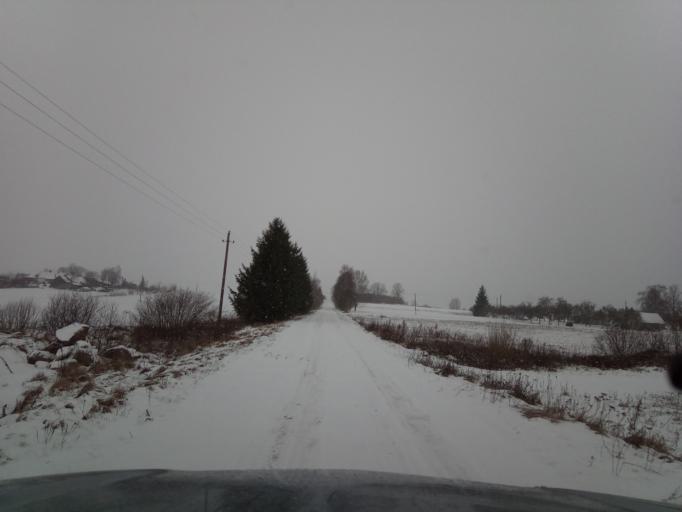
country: LT
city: Ramygala
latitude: 55.5897
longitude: 24.3511
